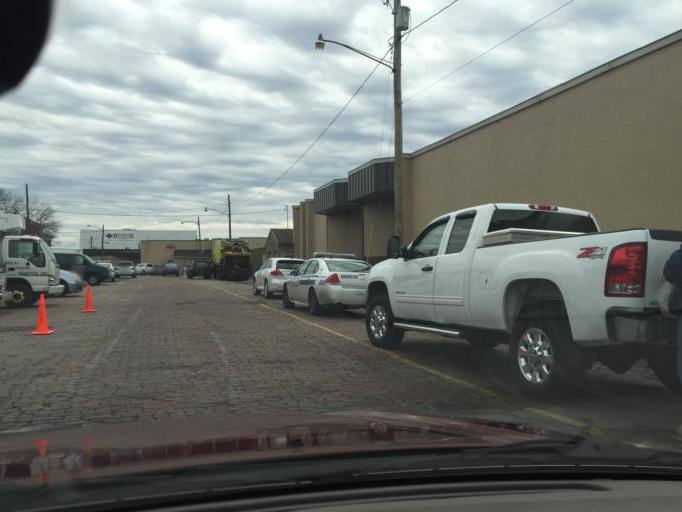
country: US
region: New York
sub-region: Monroe County
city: Rochester
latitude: 43.1649
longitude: -77.5898
